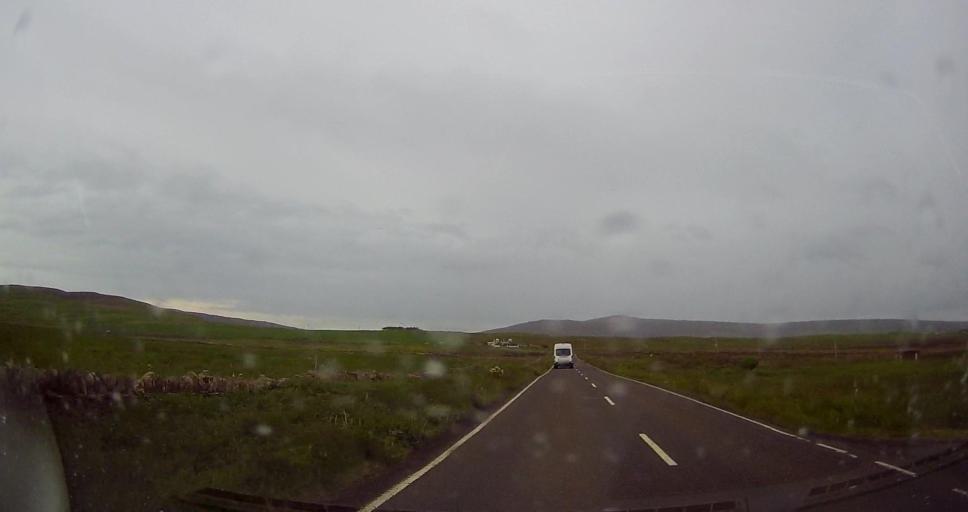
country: GB
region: Scotland
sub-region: Orkney Islands
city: Stromness
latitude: 59.0092
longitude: -3.1556
